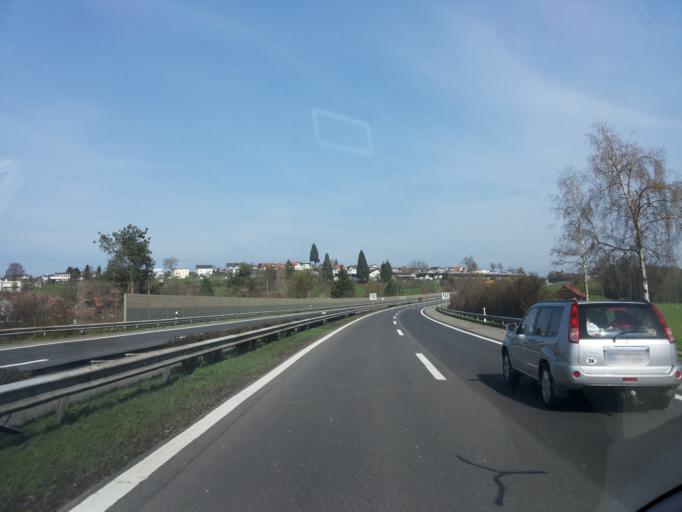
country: CH
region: Lucerne
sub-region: Sursee District
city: Knutwil
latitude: 47.1834
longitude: 8.0814
